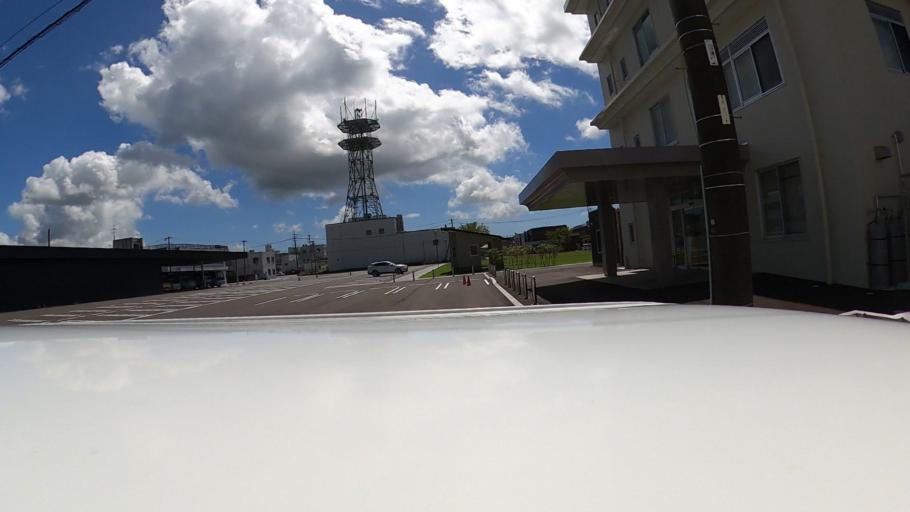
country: JP
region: Miyazaki
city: Tsuma
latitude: 32.1088
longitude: 131.4009
